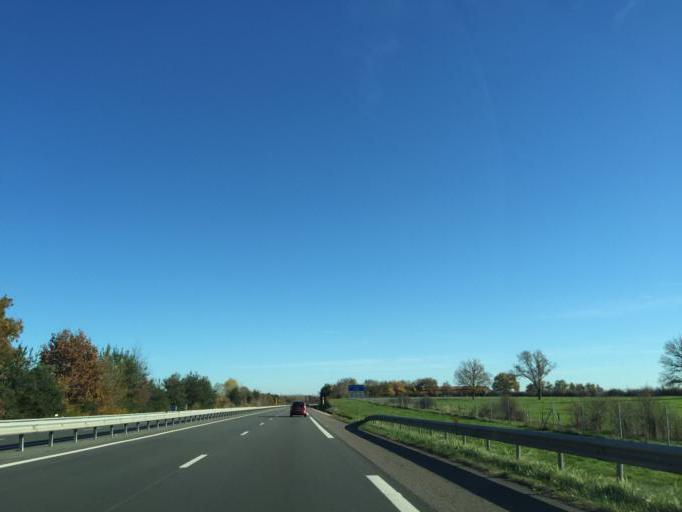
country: FR
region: Rhone-Alpes
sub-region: Departement de la Loire
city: Saint-Germain-Laval
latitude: 45.8517
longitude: 4.0676
